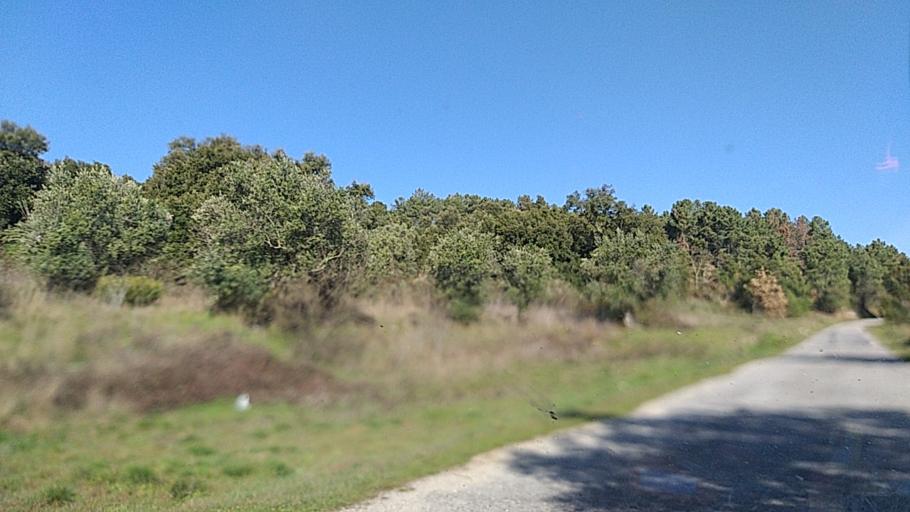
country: PT
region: Guarda
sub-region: Celorico da Beira
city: Celorico da Beira
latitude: 40.6913
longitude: -7.4535
